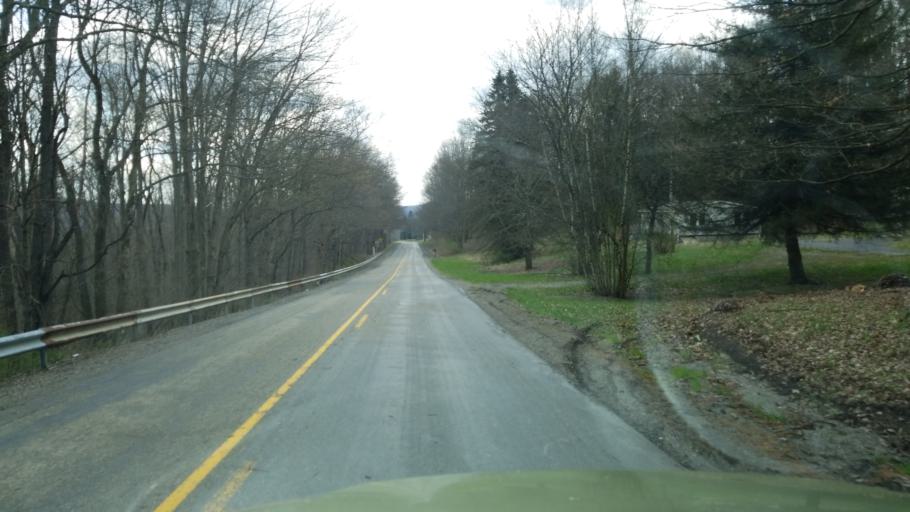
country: US
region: Pennsylvania
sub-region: Jefferson County
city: Brockway
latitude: 41.2725
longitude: -78.8192
